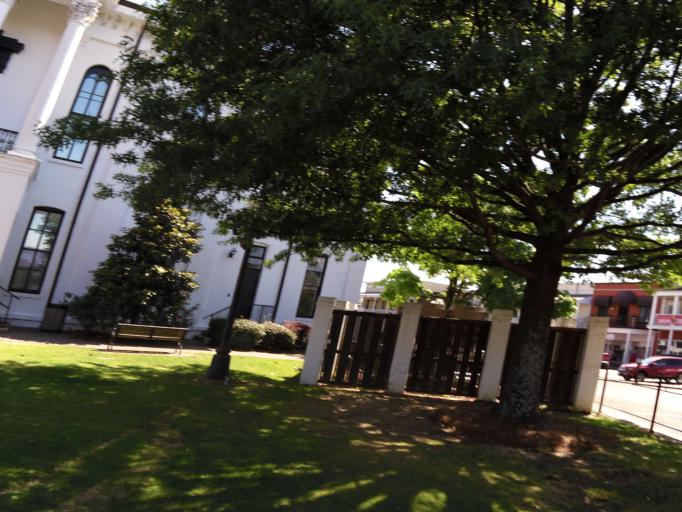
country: US
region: Mississippi
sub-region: Lafayette County
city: Oxford
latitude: 34.3666
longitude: -89.5188
